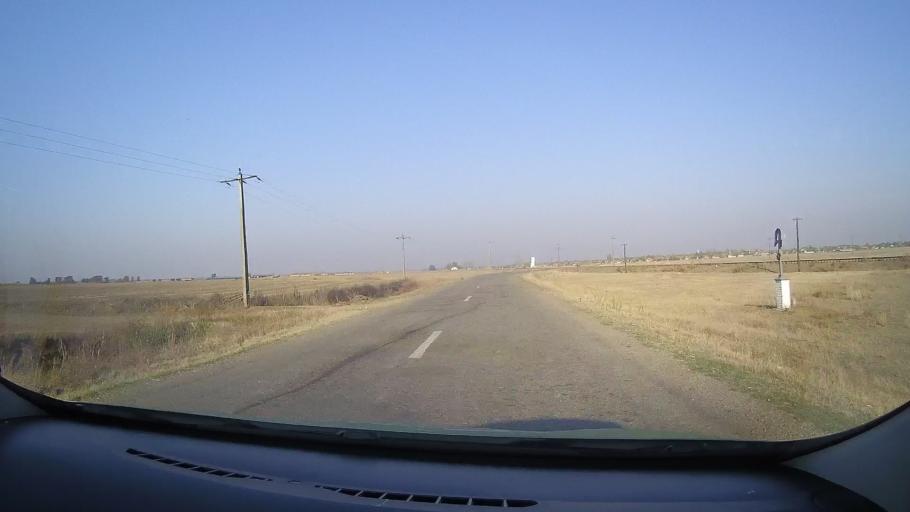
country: RO
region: Arad
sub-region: Comuna Graniceri
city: Graniceri
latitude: 46.5094
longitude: 21.3158
